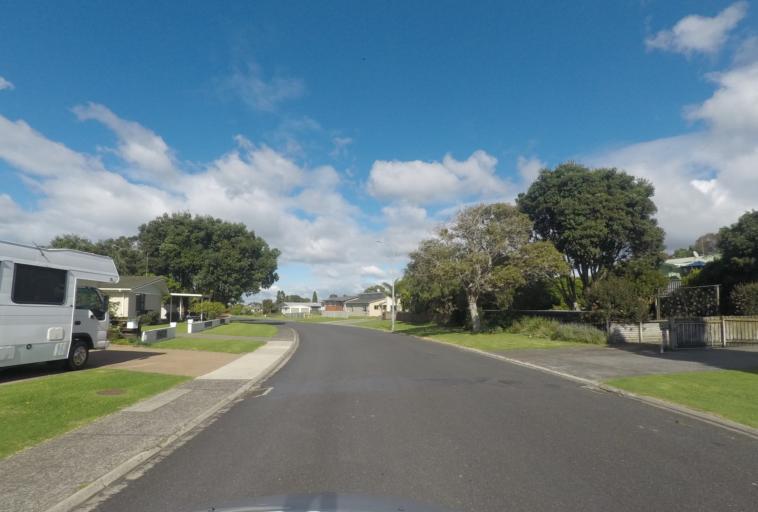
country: NZ
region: Bay of Plenty
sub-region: Western Bay of Plenty District
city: Waihi Beach
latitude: -37.4148
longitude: 175.9431
